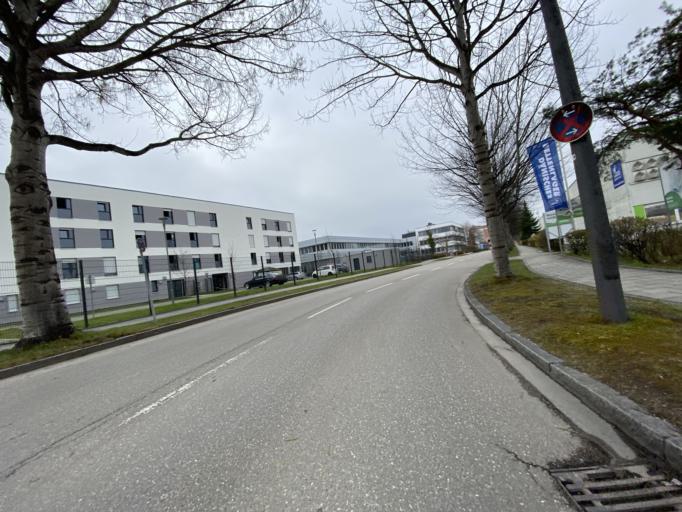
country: DE
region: Bavaria
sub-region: Upper Bavaria
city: Bogenhausen
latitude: 48.1918
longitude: 11.5964
